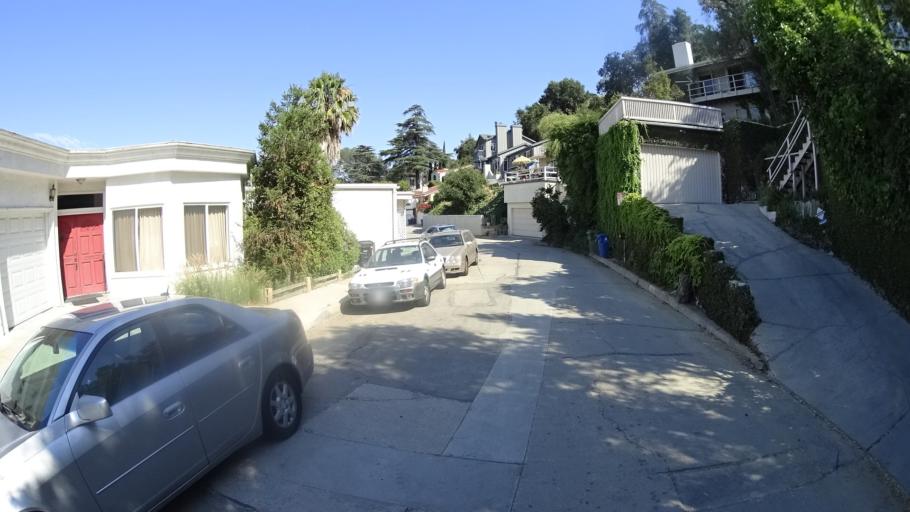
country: US
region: California
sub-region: Los Angeles County
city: North Hollywood
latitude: 34.1400
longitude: -118.3868
